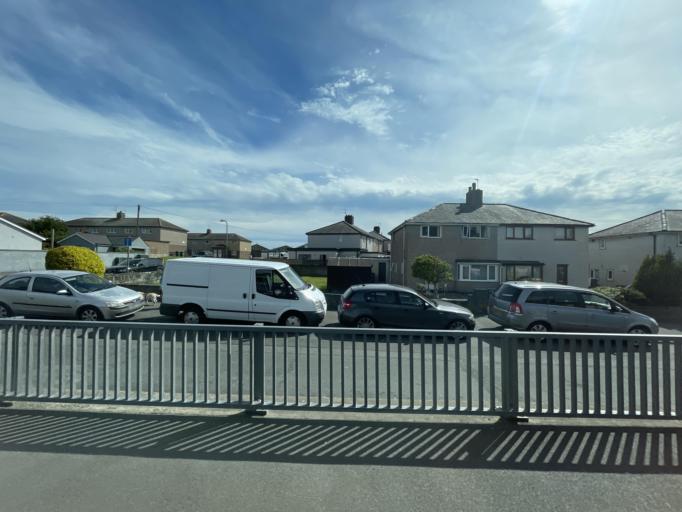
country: GB
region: Wales
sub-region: Anglesey
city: Holyhead
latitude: 53.3038
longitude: -4.6246
